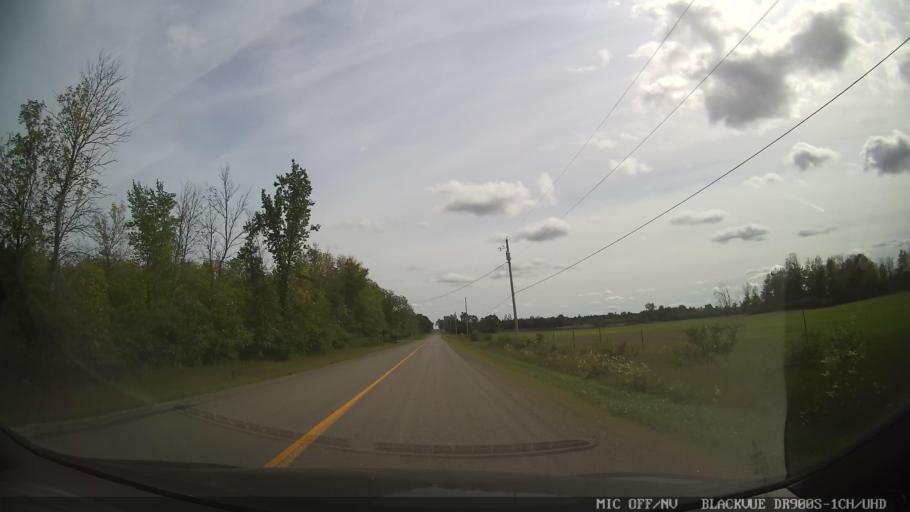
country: CA
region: Ontario
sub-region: Lanark County
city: Smiths Falls
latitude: 44.8888
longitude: -75.9204
